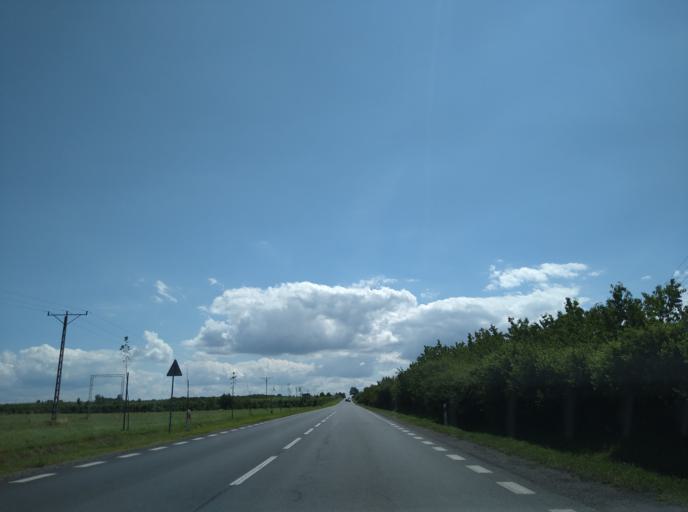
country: PL
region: Masovian Voivodeship
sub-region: Powiat piaseczynski
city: Gora Kalwaria
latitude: 51.9392
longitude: 21.2139
